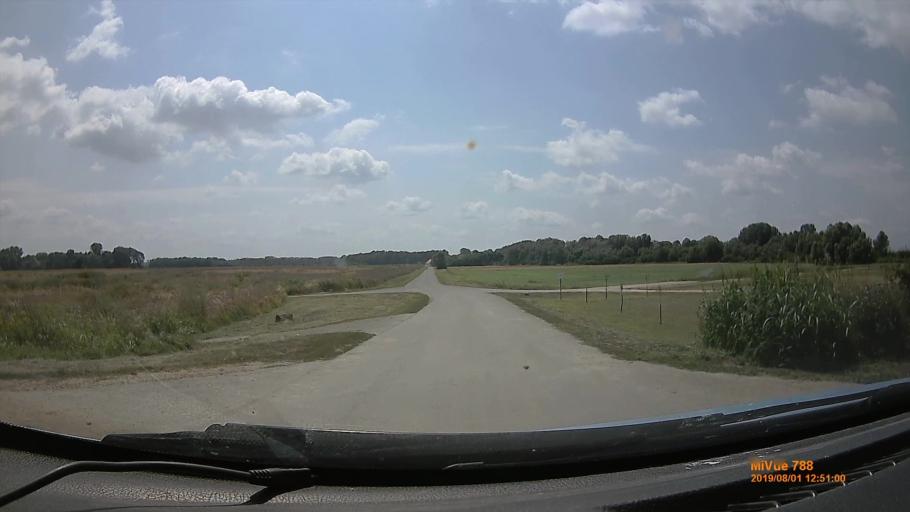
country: HR
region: Osjecko-Baranjska
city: Viljevo
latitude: 45.8065
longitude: 18.1021
